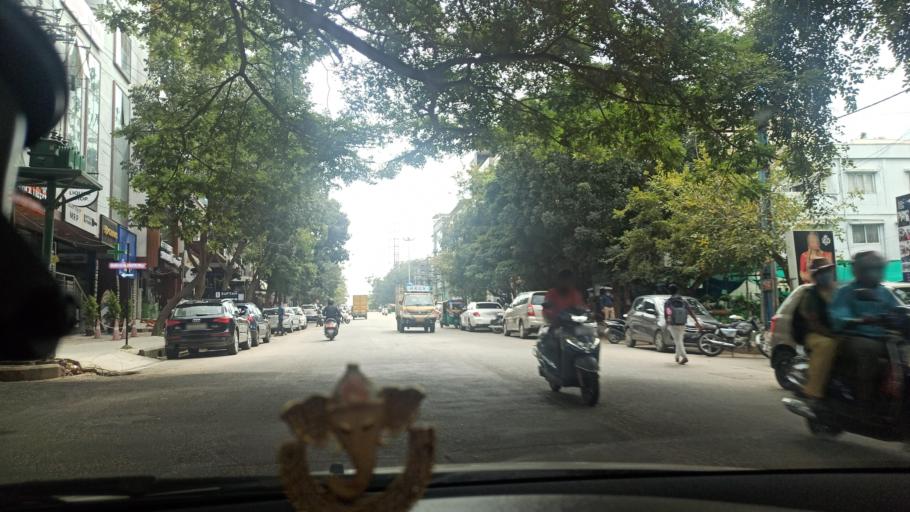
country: IN
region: Karnataka
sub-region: Bangalore Urban
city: Bangalore
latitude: 12.9135
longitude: 77.6447
